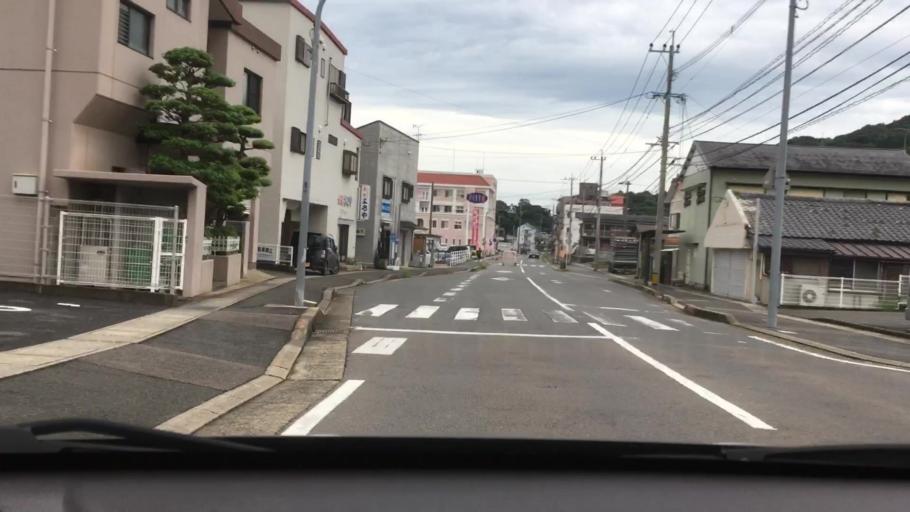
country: JP
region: Nagasaki
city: Nagasaki-shi
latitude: 32.7566
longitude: 129.9446
